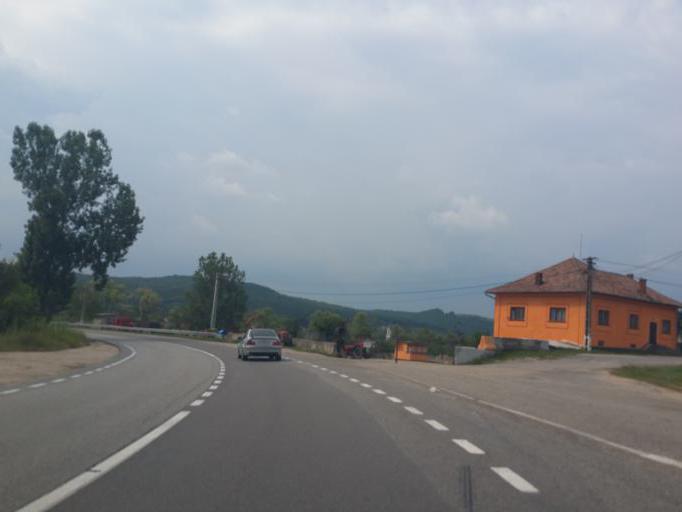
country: RO
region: Salaj
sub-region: Comuna Romanasi
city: Romanasi
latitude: 47.1075
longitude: 23.1856
